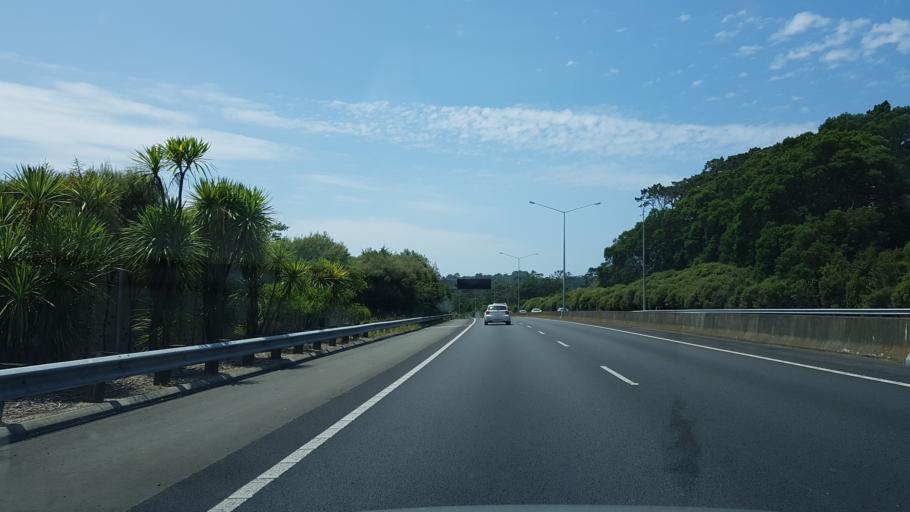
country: NZ
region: Auckland
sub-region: Auckland
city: North Shore
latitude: -36.7794
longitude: 174.6800
